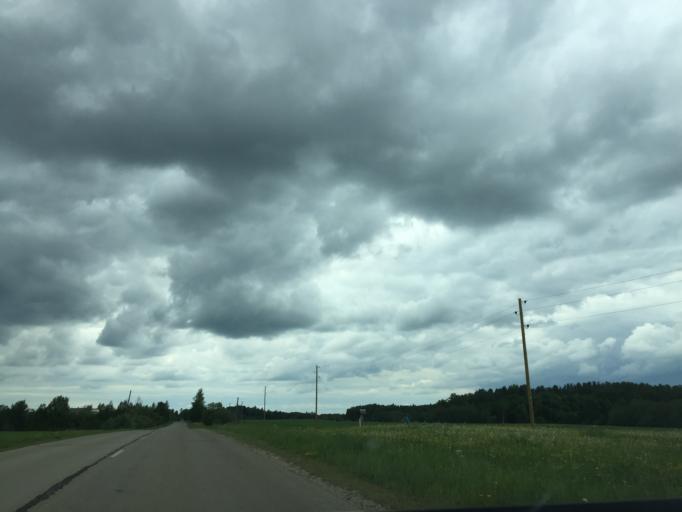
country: LV
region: Dagda
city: Dagda
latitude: 56.1090
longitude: 27.4887
